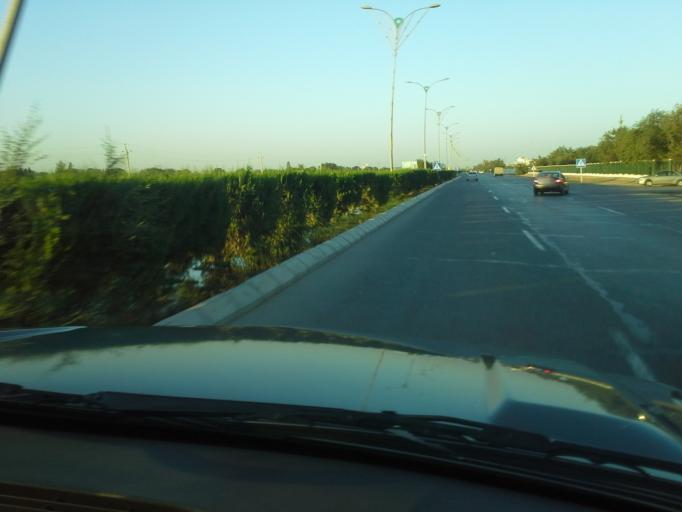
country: TM
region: Dasoguz
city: Dasoguz
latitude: 41.8074
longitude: 59.9067
